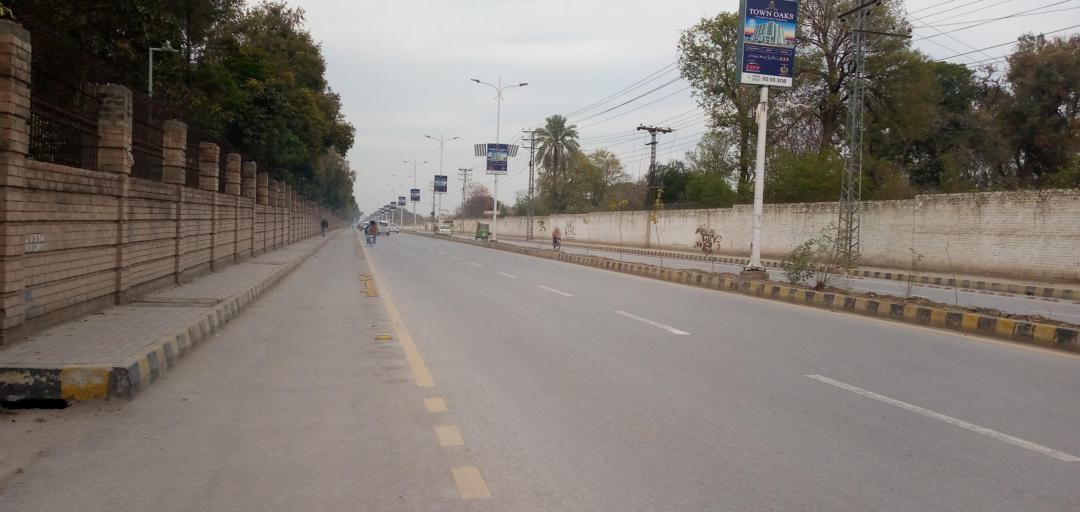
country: PK
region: Khyber Pakhtunkhwa
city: Peshawar
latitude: 34.0007
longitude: 71.4885
